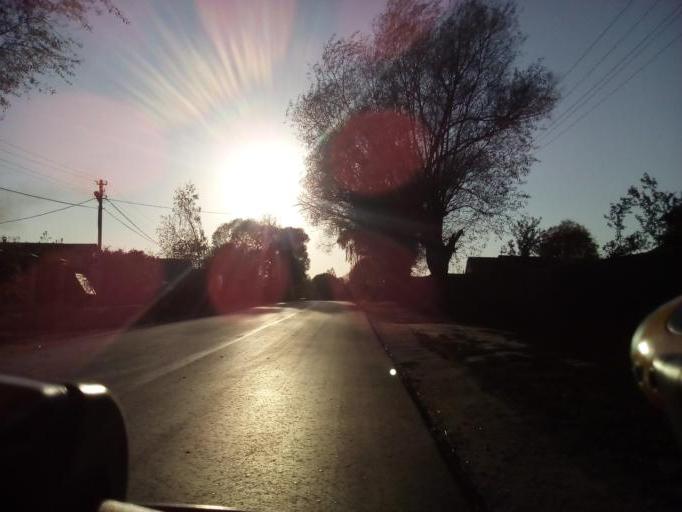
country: RU
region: Moskovskaya
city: Ramenskoye
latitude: 55.6123
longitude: 38.2943
